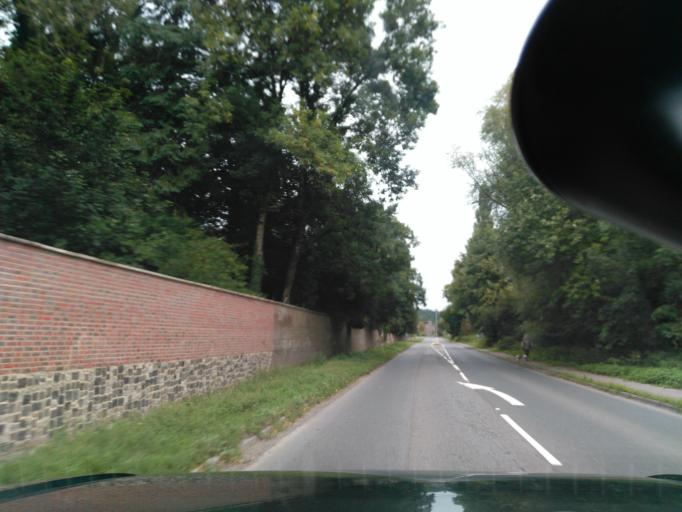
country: GB
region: England
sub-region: Wiltshire
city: Warminster
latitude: 51.1678
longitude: -2.1899
